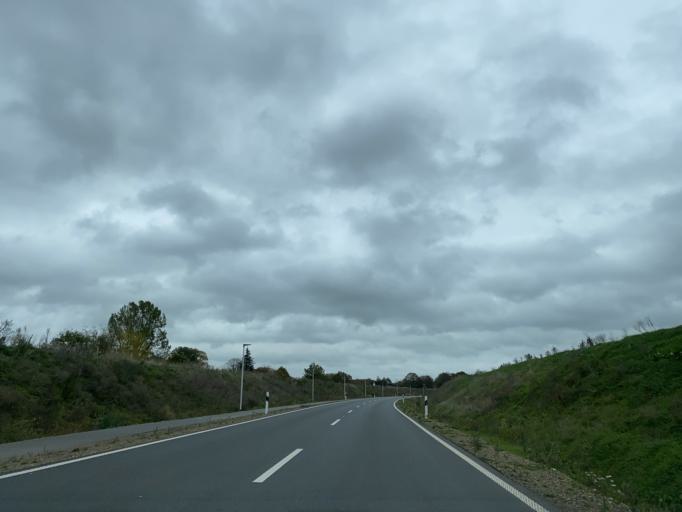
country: DE
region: Schleswig-Holstein
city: Tastrup
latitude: 54.7768
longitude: 9.4818
